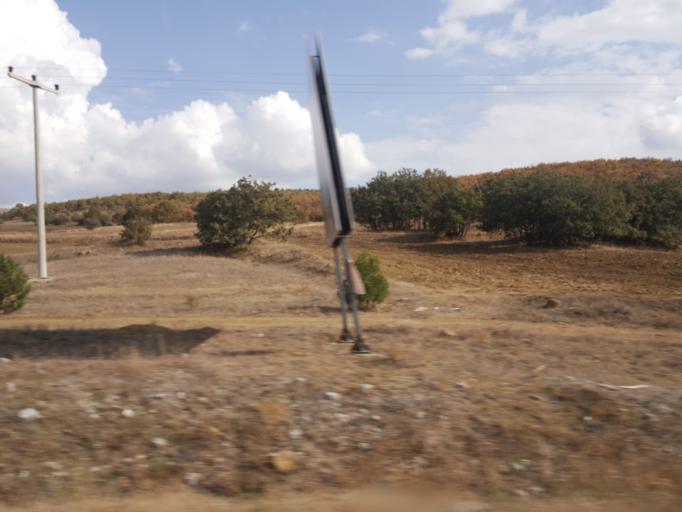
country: TR
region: Corum
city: Alaca
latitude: 40.2809
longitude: 34.6462
